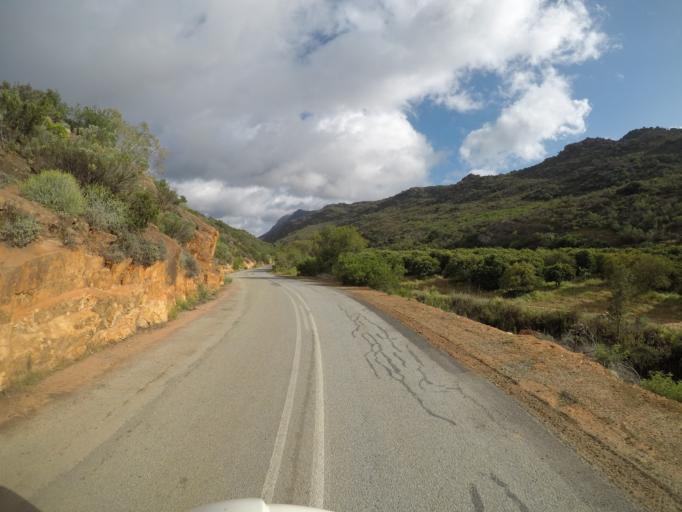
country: ZA
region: Western Cape
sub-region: West Coast District Municipality
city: Clanwilliam
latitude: -32.4172
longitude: 18.9262
